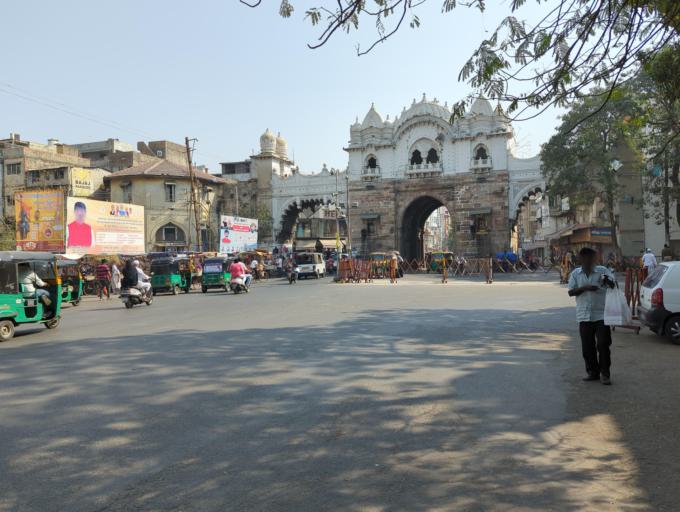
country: IN
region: Gujarat
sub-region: Vadodara
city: Vadodara
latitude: 22.3000
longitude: 73.2063
